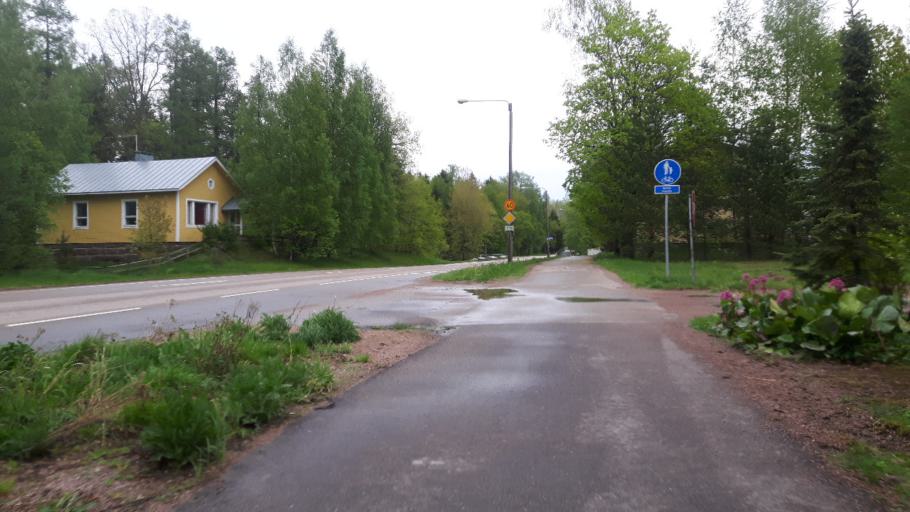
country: FI
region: Kymenlaakso
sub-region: Kotka-Hamina
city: Hamina
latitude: 60.5655
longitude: 27.0959
